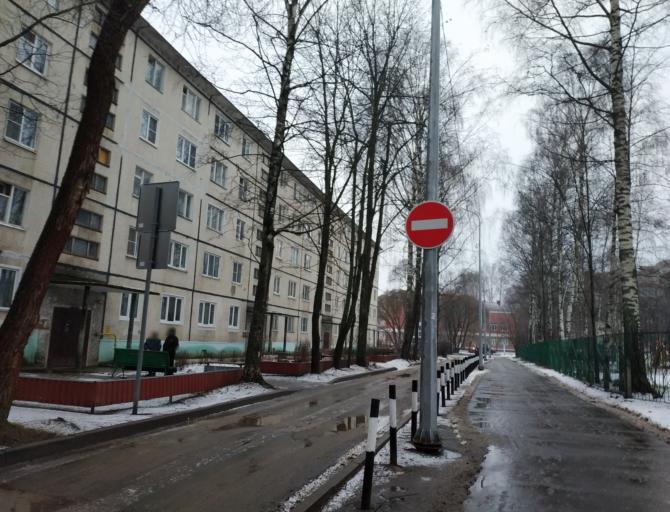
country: RU
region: Moskovskaya
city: Taldom
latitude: 56.7409
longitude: 37.5378
